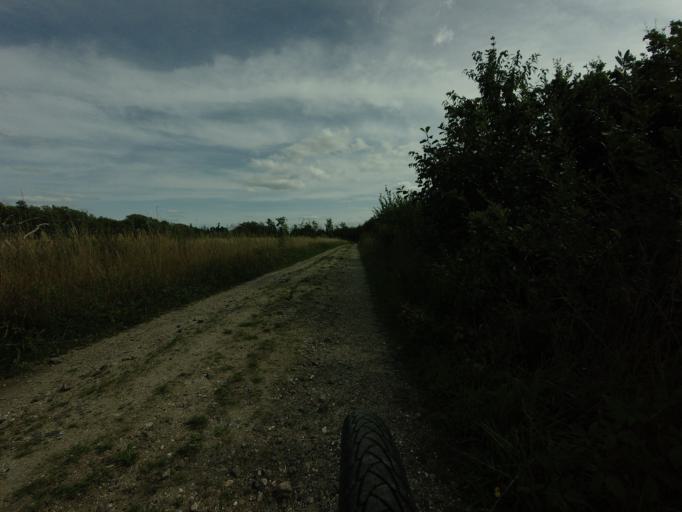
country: DK
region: Zealand
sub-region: Faxe Kommune
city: Fakse Ladeplads
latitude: 55.2273
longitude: 12.1892
